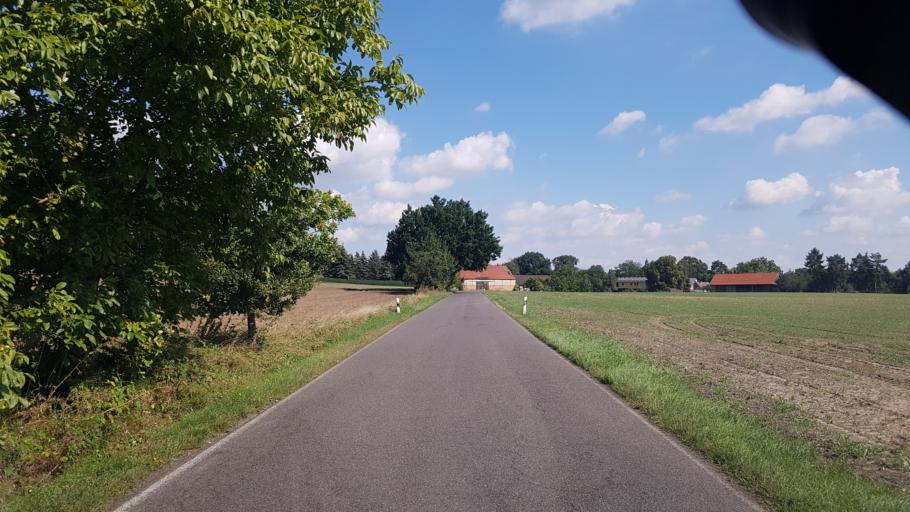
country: DE
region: Brandenburg
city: Drebkau
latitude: 51.6688
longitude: 14.2263
